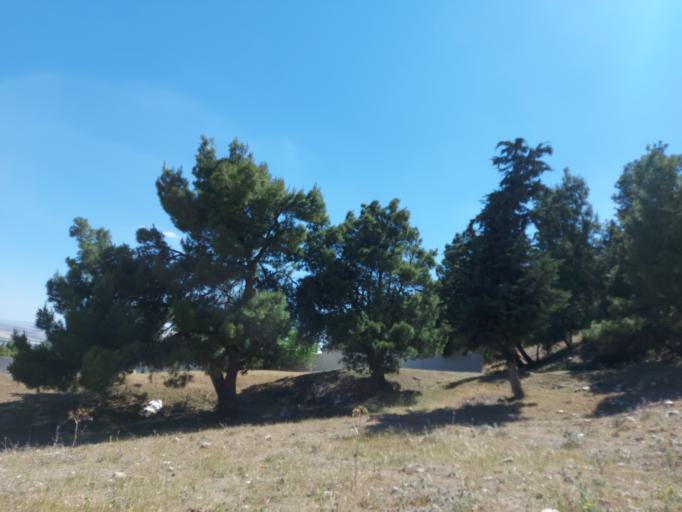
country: TN
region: Kef
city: El Kef
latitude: 36.1843
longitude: 8.7256
